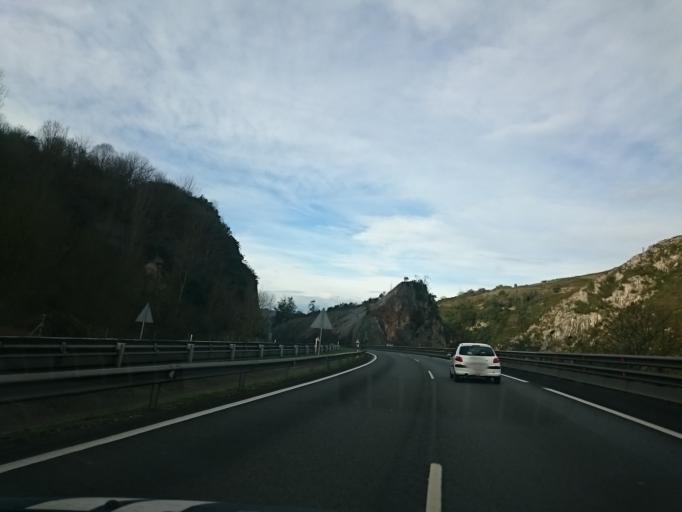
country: ES
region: Asturias
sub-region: Province of Asturias
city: Castandiello
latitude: 43.3002
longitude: -5.8478
